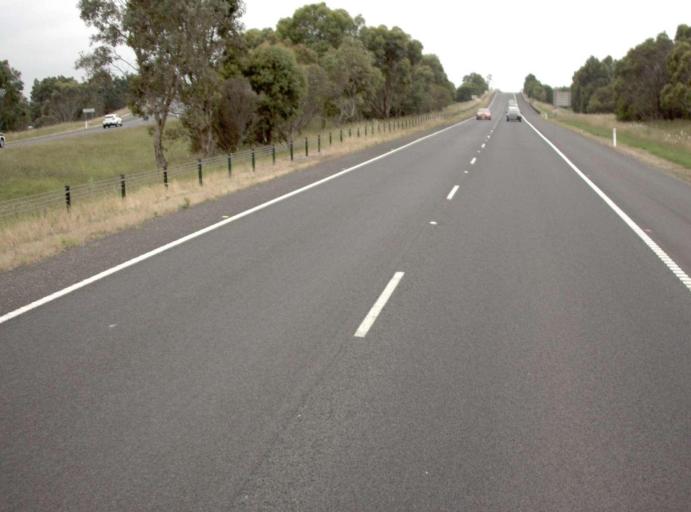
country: AU
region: Victoria
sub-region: Latrobe
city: Morwell
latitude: -38.2334
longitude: 146.4552
